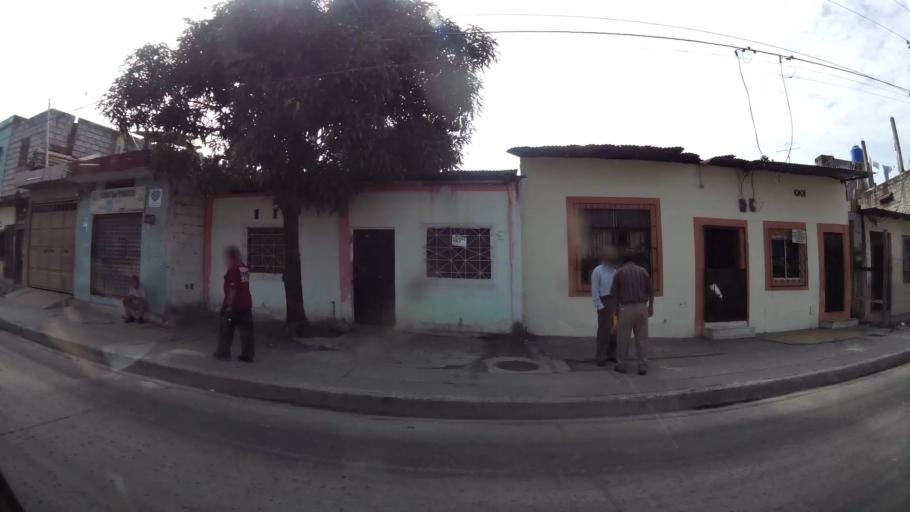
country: EC
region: Guayas
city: Guayaquil
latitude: -2.2558
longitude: -79.8792
